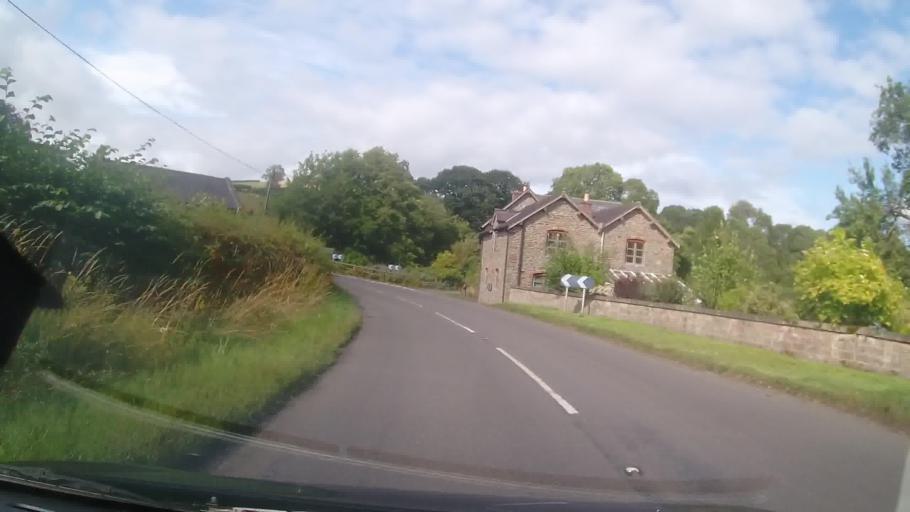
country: GB
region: Wales
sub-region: Sir Powys
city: Knighton
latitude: 52.3835
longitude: -3.0388
